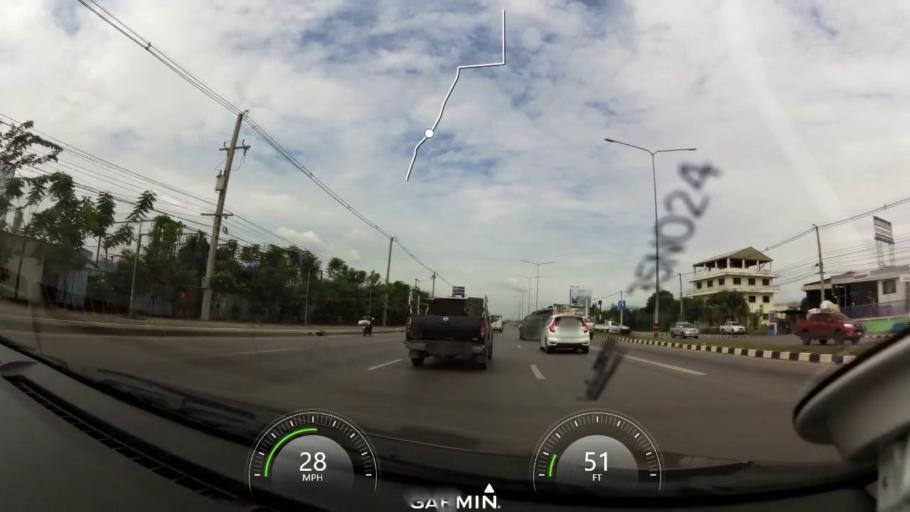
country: TH
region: Samut Sakhon
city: Krathum Baen
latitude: 13.6587
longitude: 100.3093
